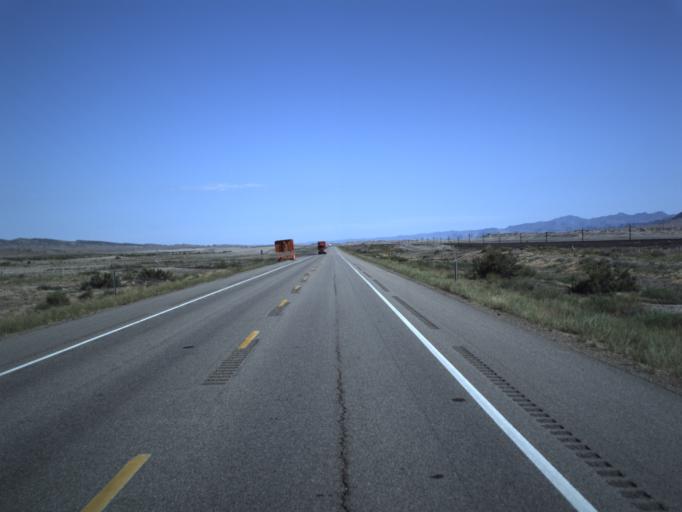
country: US
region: Utah
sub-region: Carbon County
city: East Carbon City
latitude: 39.1004
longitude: -110.3236
